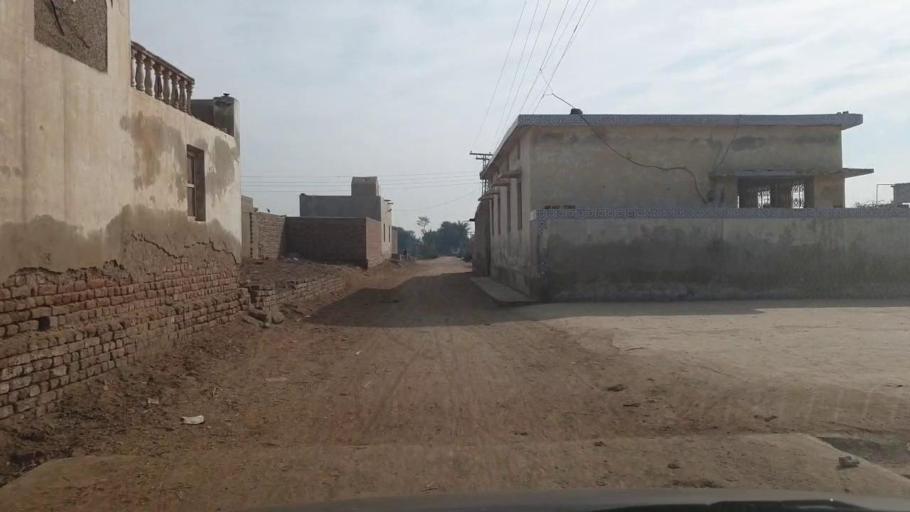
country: PK
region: Sindh
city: Shahpur Chakar
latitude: 26.1747
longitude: 68.5935
